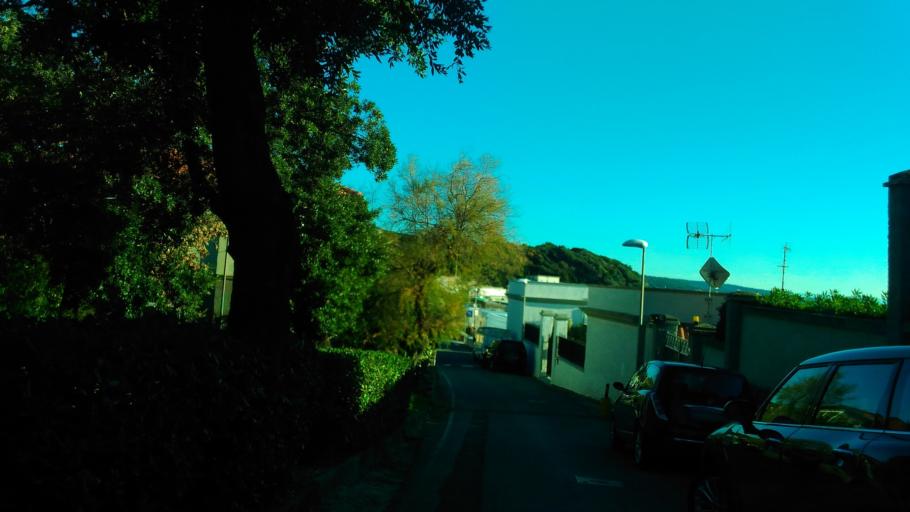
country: IT
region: Tuscany
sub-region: Provincia di Livorno
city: Quercianella
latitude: 43.4593
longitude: 10.3636
